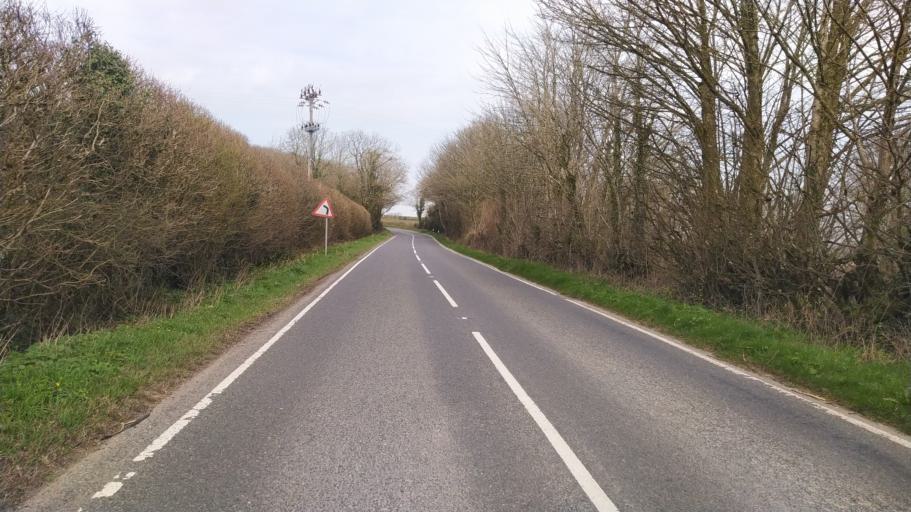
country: GB
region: England
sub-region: Dorset
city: Beaminster
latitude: 50.8192
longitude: -2.6610
